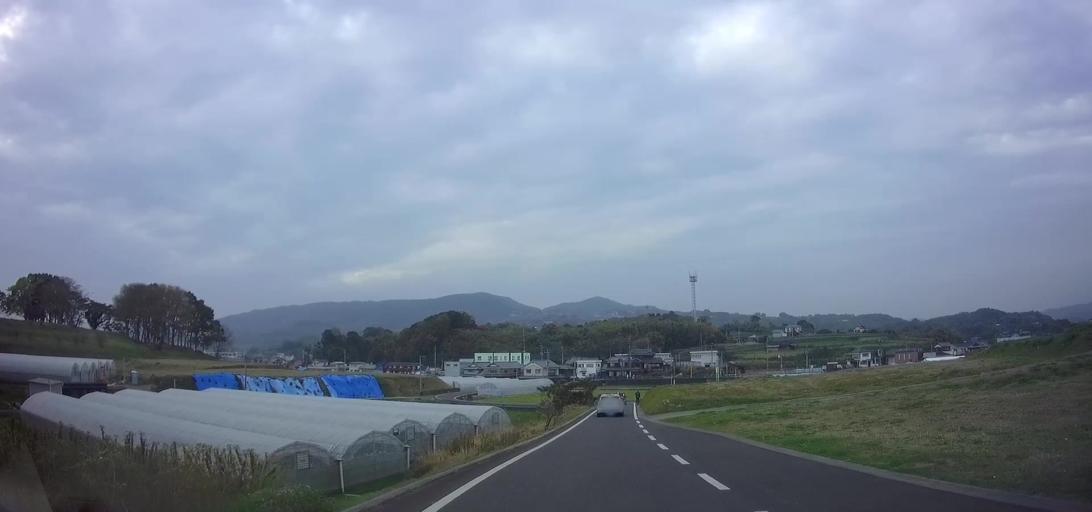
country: JP
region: Nagasaki
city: Shimabara
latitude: 32.6346
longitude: 130.2555
